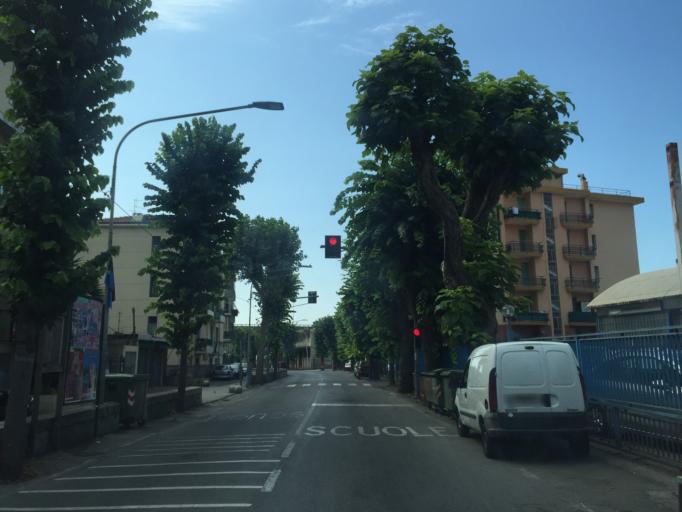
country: IT
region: Liguria
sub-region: Provincia di Imperia
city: Ventimiglia
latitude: 43.8032
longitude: 7.5979
